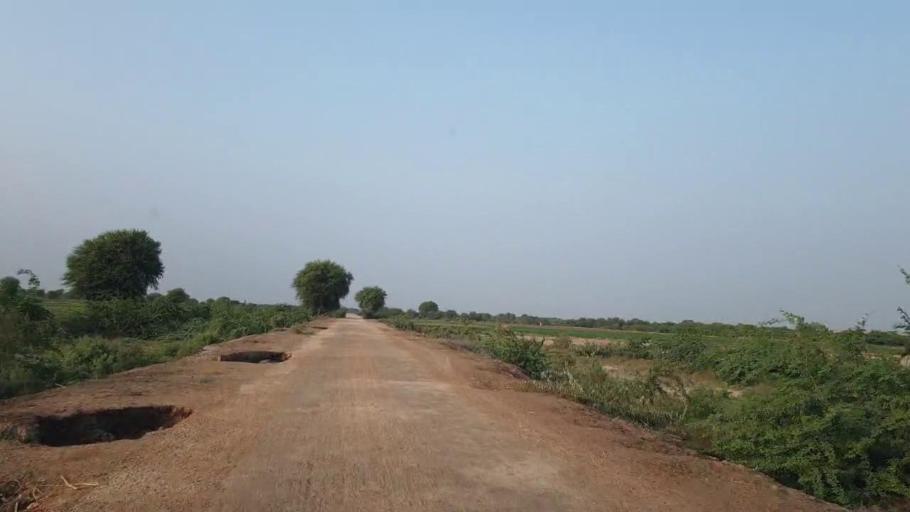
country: PK
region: Sindh
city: Rajo Khanani
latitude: 25.0299
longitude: 68.9773
